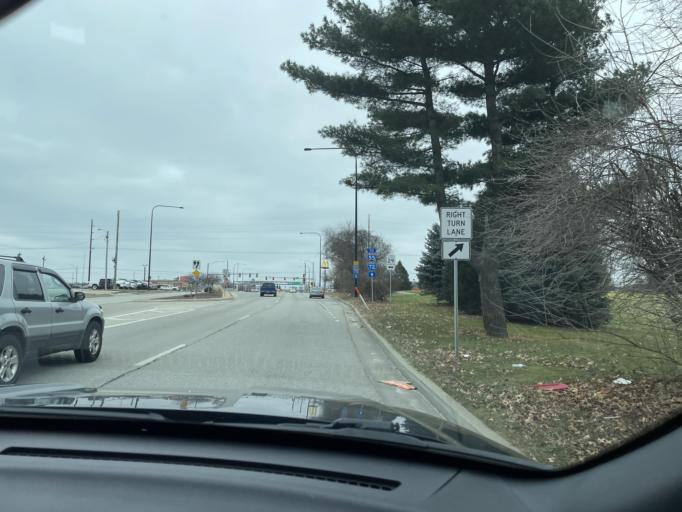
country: US
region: Illinois
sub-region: Sangamon County
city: Grandview
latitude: 39.8019
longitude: -89.6082
